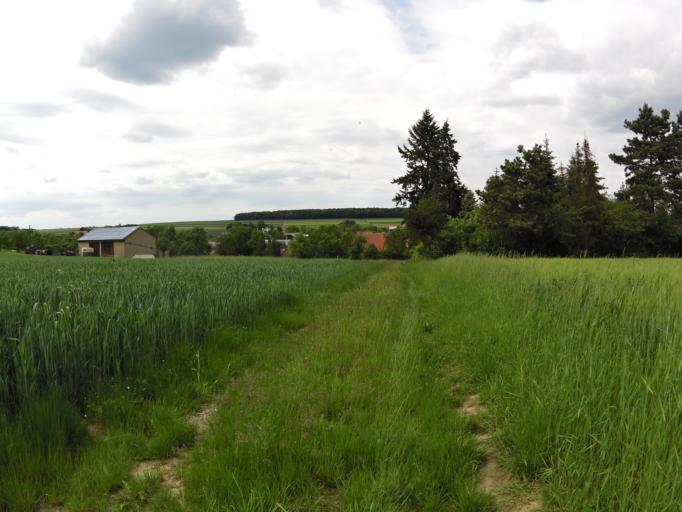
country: DE
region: Bavaria
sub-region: Regierungsbezirk Unterfranken
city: Theilheim
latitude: 49.7312
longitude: 10.0364
